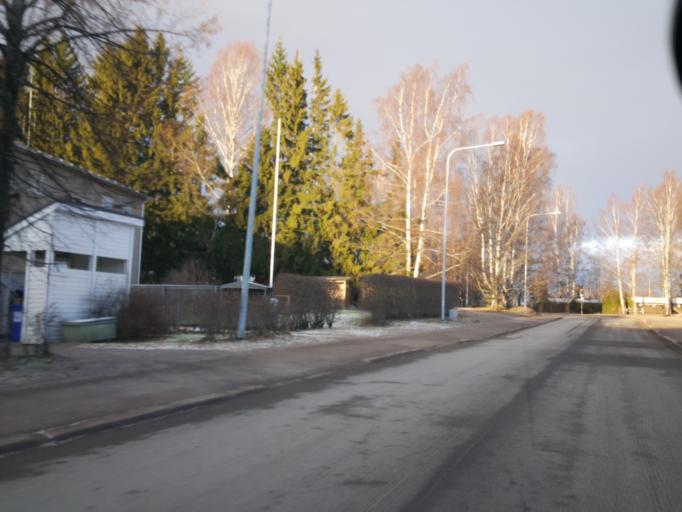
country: FI
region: Uusimaa
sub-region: Helsinki
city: Vantaa
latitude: 60.2487
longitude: 24.9894
